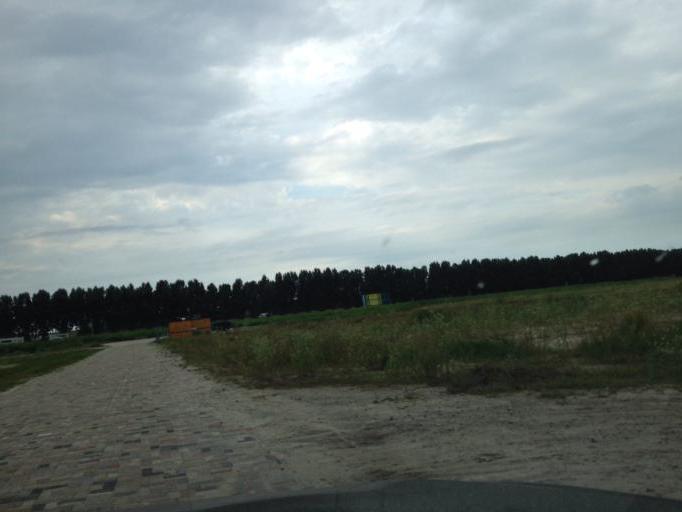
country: NL
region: Flevoland
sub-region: Gemeente Almere
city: Almere Stad
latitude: 52.3597
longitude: 5.2771
